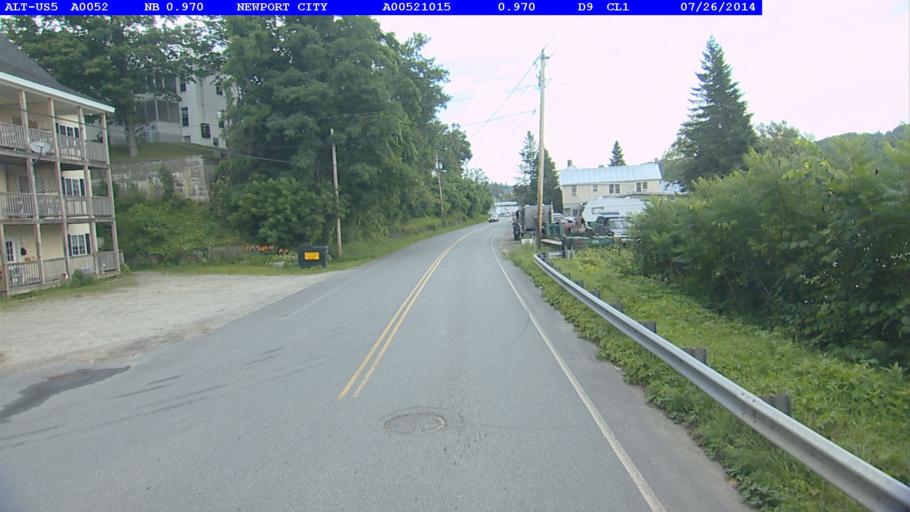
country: US
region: Vermont
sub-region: Orleans County
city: Newport
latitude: 44.9325
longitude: -72.2088
